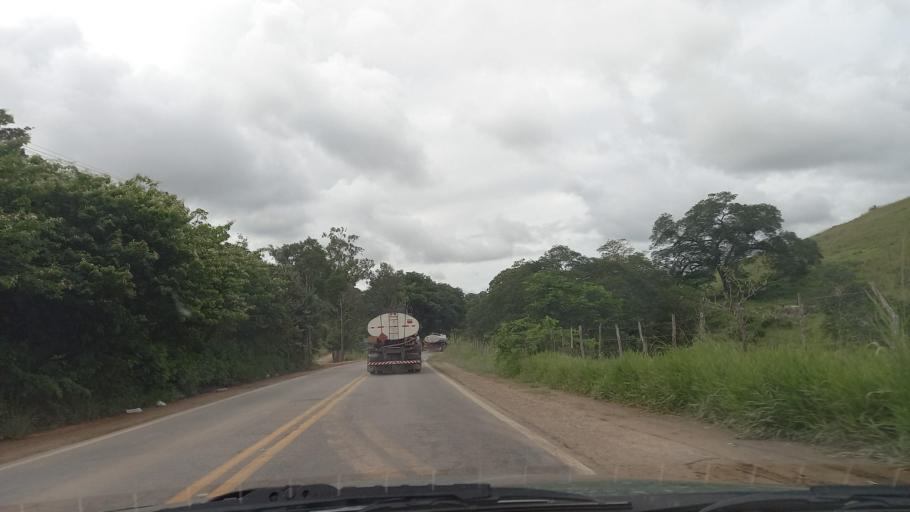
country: BR
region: Pernambuco
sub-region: Canhotinho
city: Canhotinho
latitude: -8.8684
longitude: -36.1931
